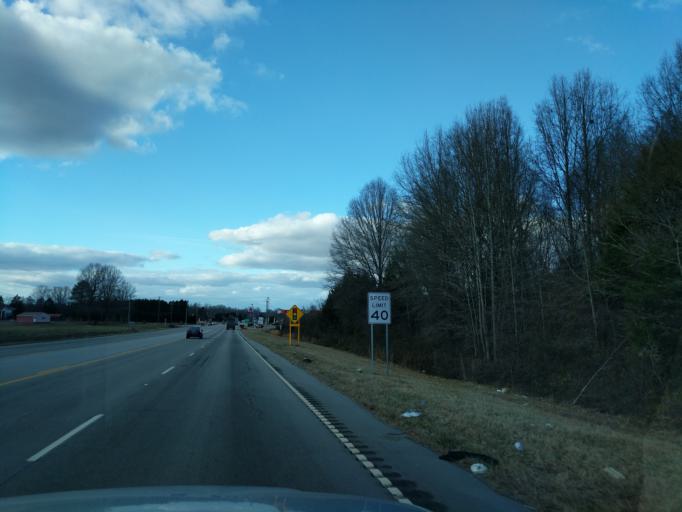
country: US
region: South Carolina
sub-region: Greenville County
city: Five Forks
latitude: 34.8105
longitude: -82.1321
